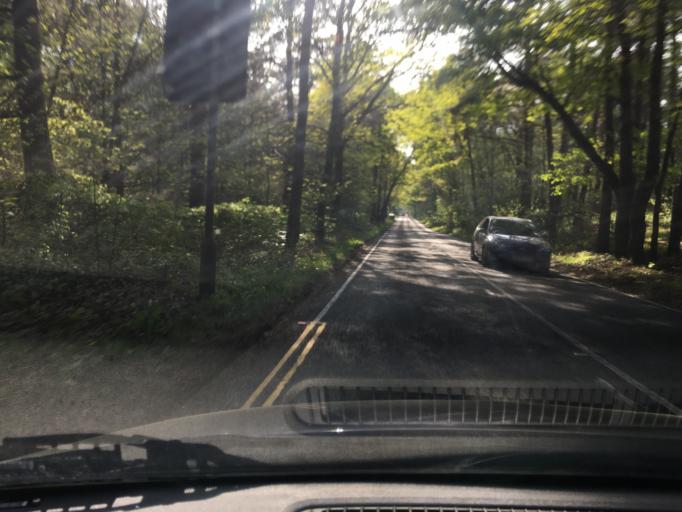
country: GB
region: England
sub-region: Bracknell Forest
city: Bracknell
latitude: 51.3876
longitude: -0.7445
